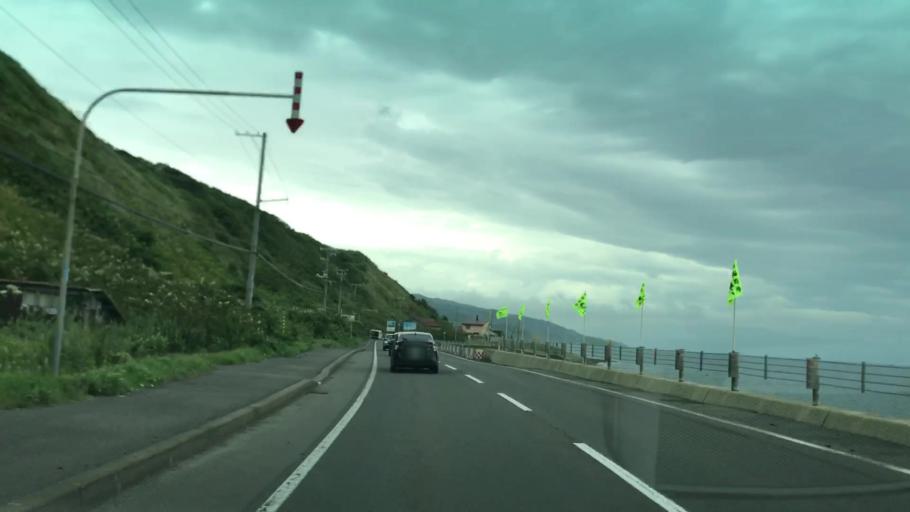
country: JP
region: Hokkaido
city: Iwanai
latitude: 42.8721
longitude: 140.3582
